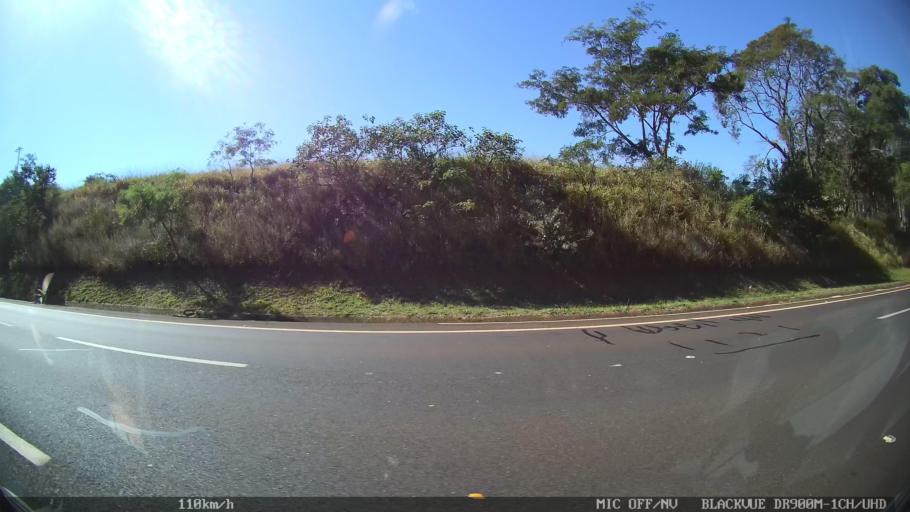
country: BR
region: Sao Paulo
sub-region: Batatais
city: Batatais
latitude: -20.8429
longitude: -47.6014
